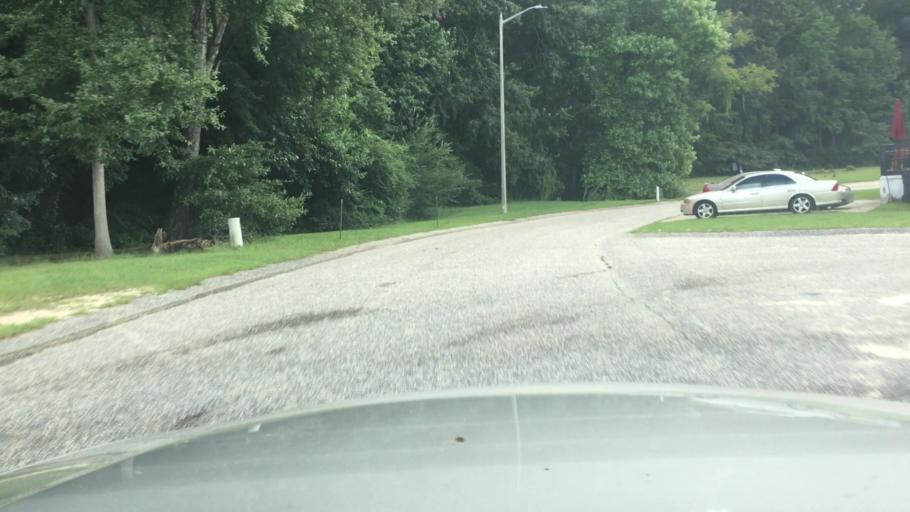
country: US
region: North Carolina
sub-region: Cumberland County
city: Hope Mills
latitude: 35.0379
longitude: -78.9769
